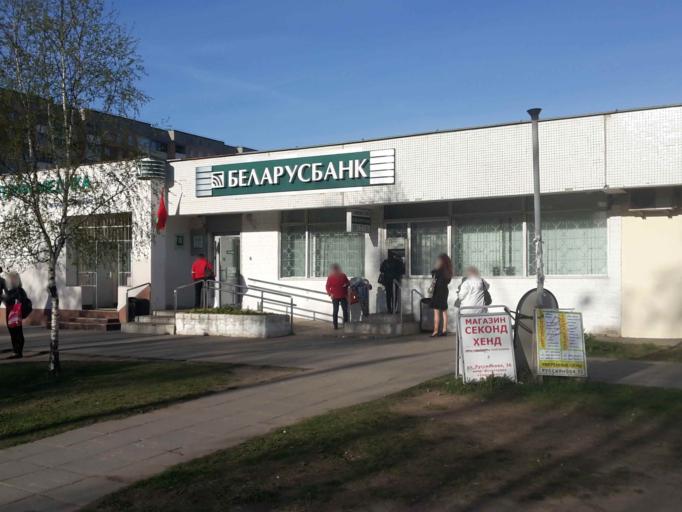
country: BY
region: Minsk
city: Borovlyany
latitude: 53.9354
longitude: 27.6882
